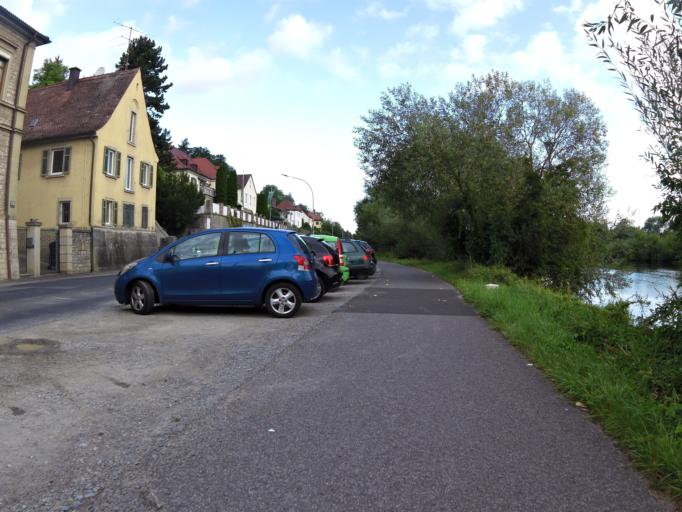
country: DE
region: Bavaria
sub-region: Regierungsbezirk Unterfranken
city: Kitzingen
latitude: 49.7449
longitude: 10.1597
